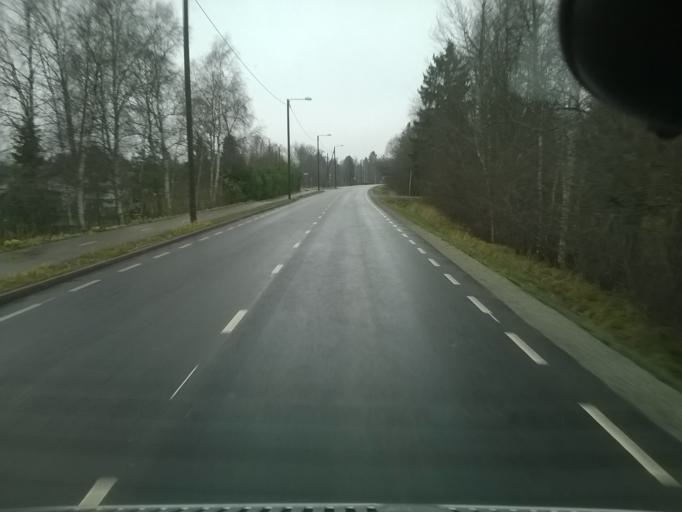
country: EE
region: Harju
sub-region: Saku vald
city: Saku
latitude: 59.2079
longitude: 24.6641
